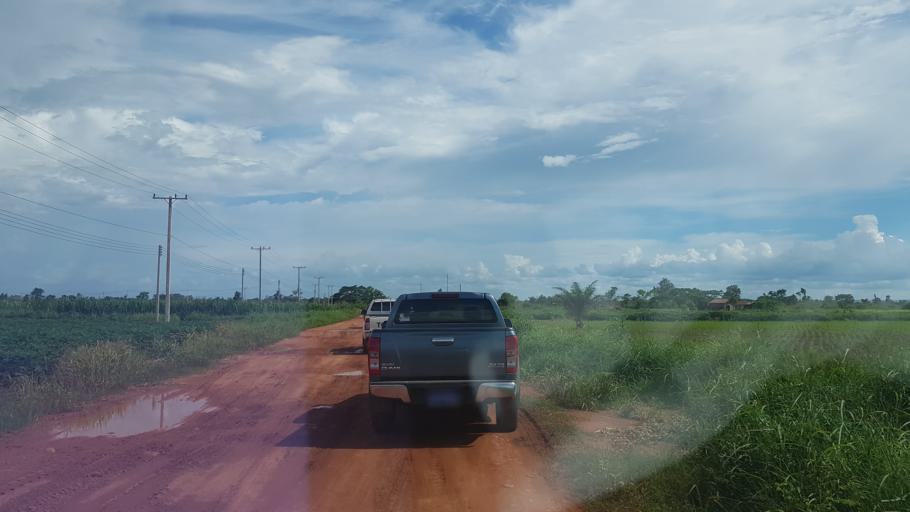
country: LA
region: Vientiane
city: Vientiane
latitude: 18.2121
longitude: 102.5661
